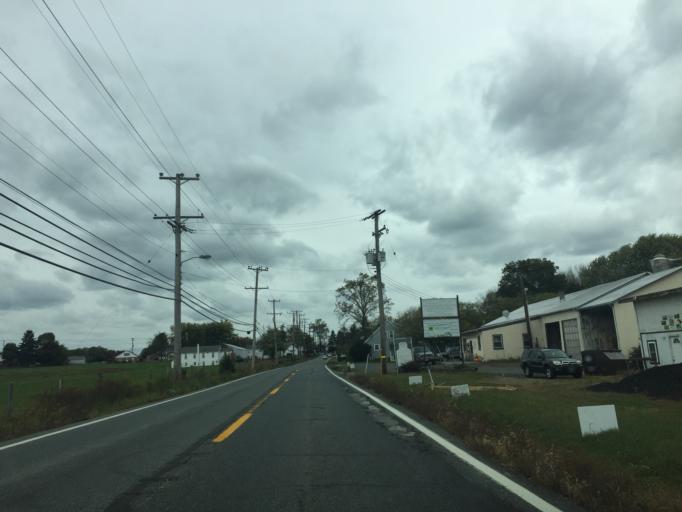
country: US
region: Maryland
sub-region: Harford County
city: Riverside
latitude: 39.5554
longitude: -76.2528
